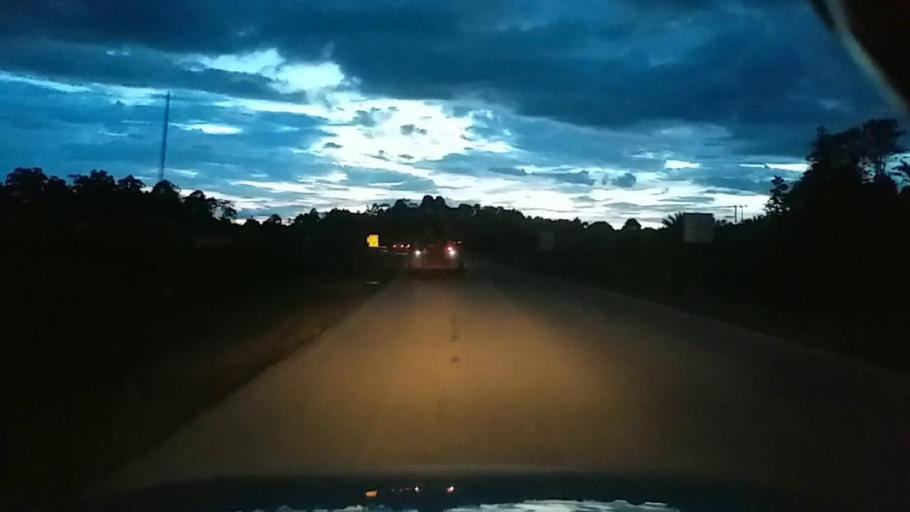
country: MY
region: Sarawak
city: Sibu
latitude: 2.4135
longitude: 112.1588
